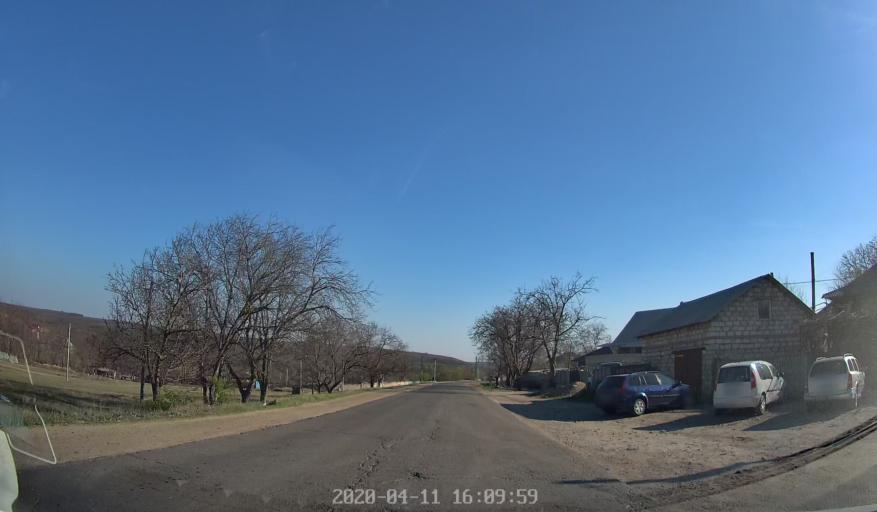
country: MD
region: Chisinau
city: Vadul lui Voda
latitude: 47.0705
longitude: 29.1360
